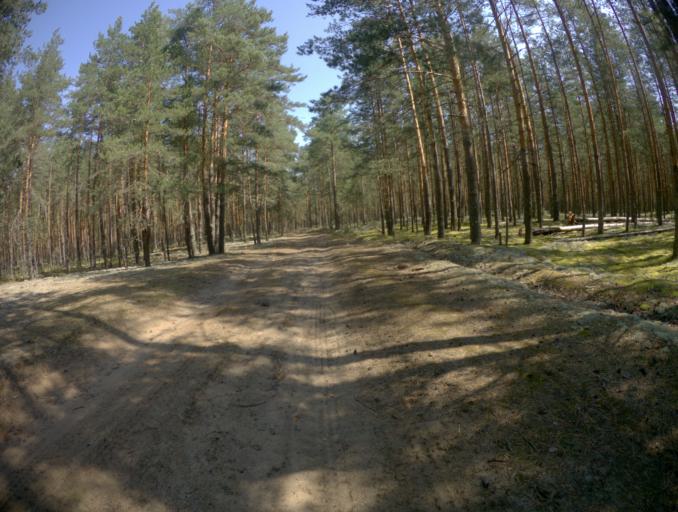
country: RU
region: Ivanovo
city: Talitsy
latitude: 56.3963
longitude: 42.2626
